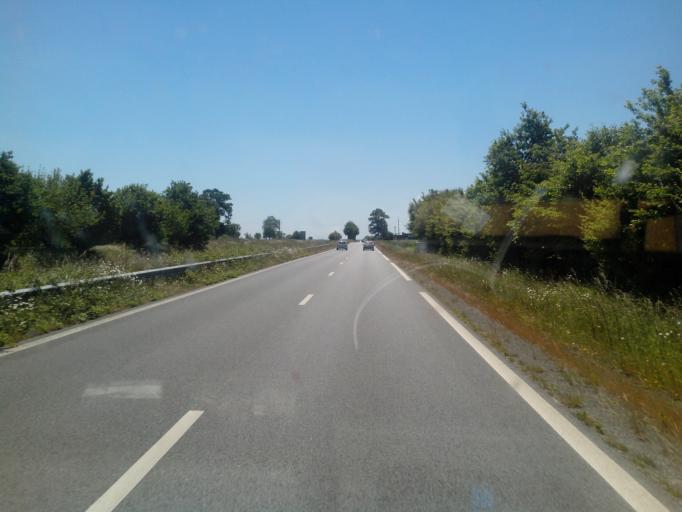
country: FR
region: Brittany
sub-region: Departement d'Ille-et-Vilaine
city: Chevaigne
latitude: 48.2191
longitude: -1.6235
